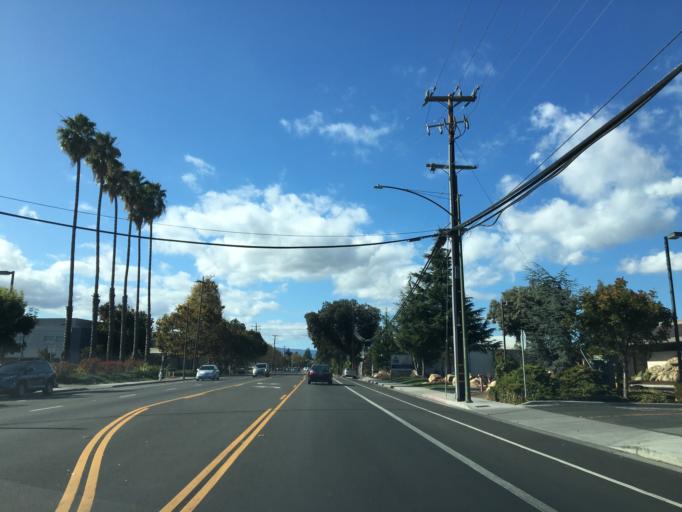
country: US
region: California
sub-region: Santa Clara County
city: Mountain View
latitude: 37.4217
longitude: -122.0972
